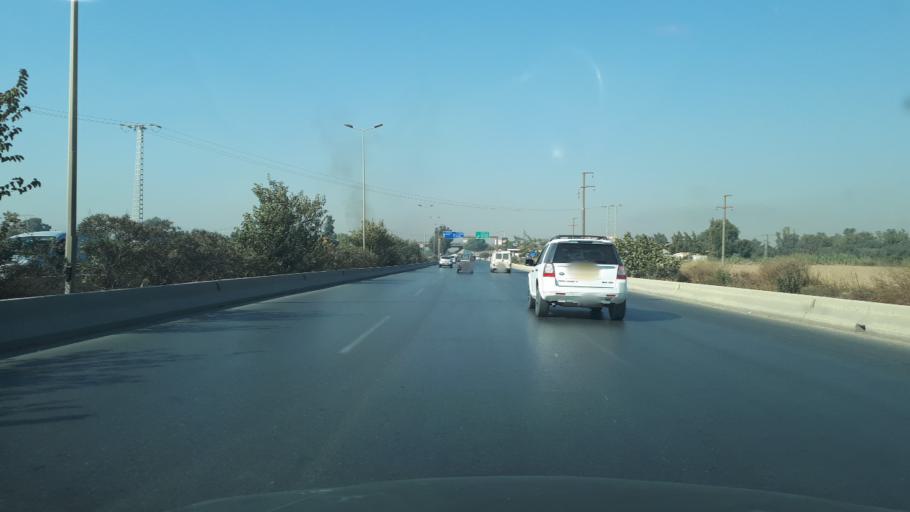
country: DZ
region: Tipaza
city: Baraki
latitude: 36.6891
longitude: 3.1181
